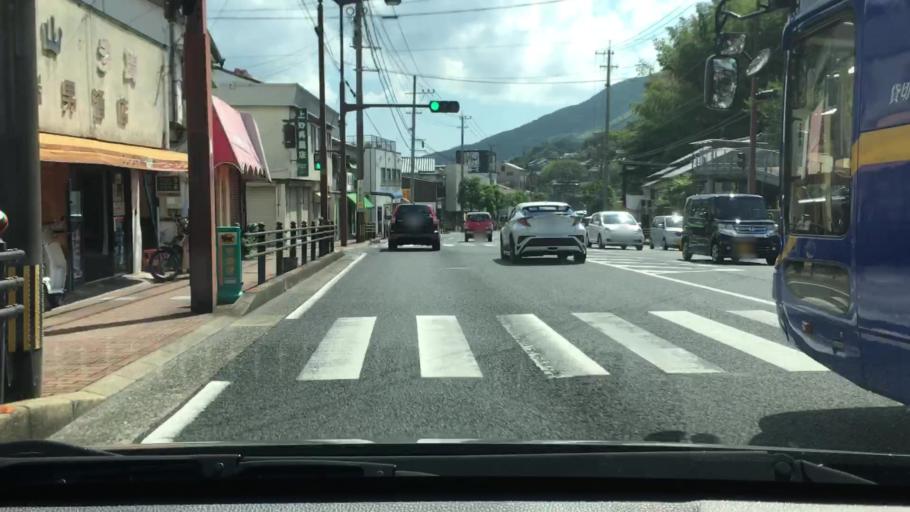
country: JP
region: Nagasaki
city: Sasebo
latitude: 33.1965
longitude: 129.7224
